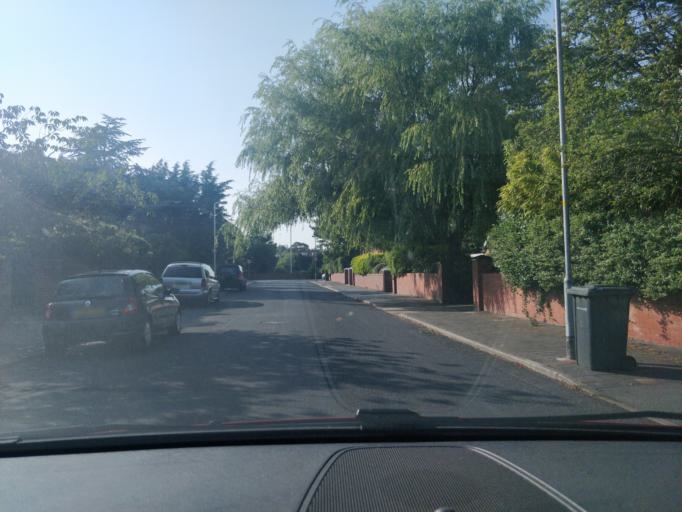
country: GB
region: England
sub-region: Sefton
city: Southport
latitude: 53.6569
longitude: -2.9812
